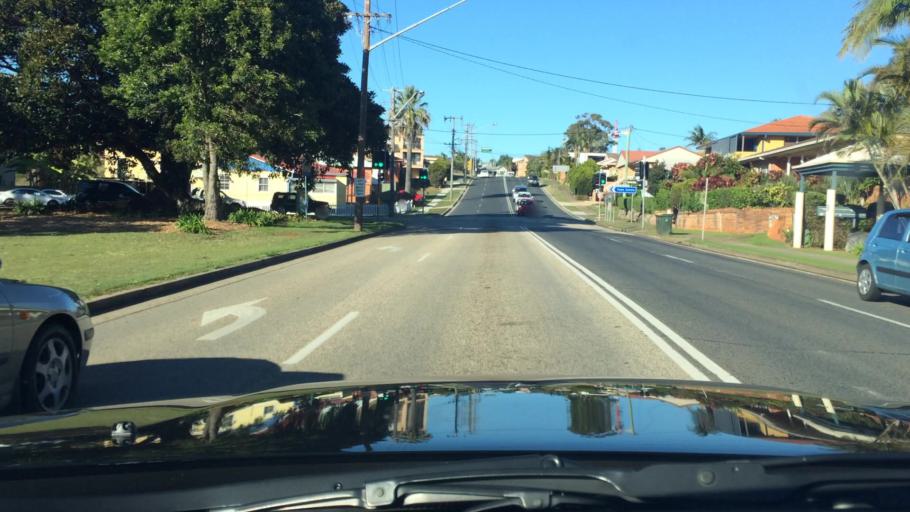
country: AU
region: New South Wales
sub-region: Port Macquarie-Hastings
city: Port Macquarie
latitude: -31.4308
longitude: 152.8998
